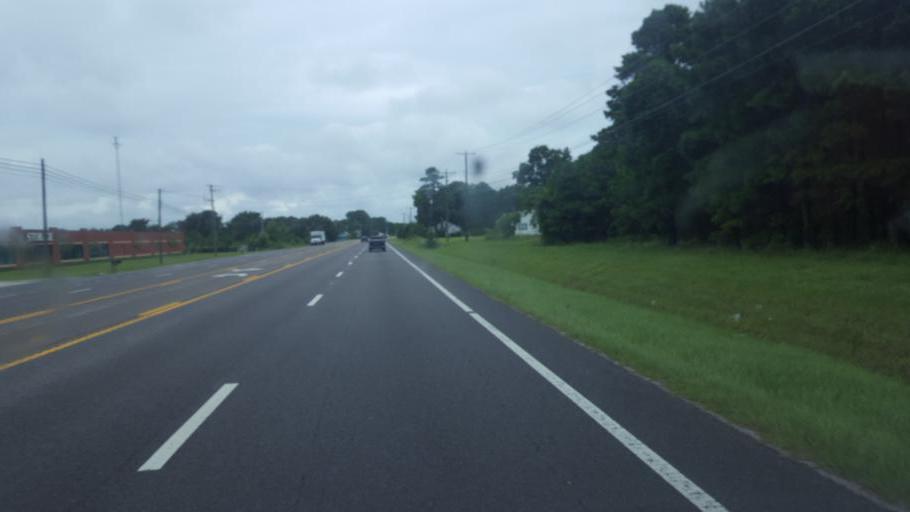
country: US
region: North Carolina
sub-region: Dare County
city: Southern Shores
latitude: 36.1171
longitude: -75.8300
